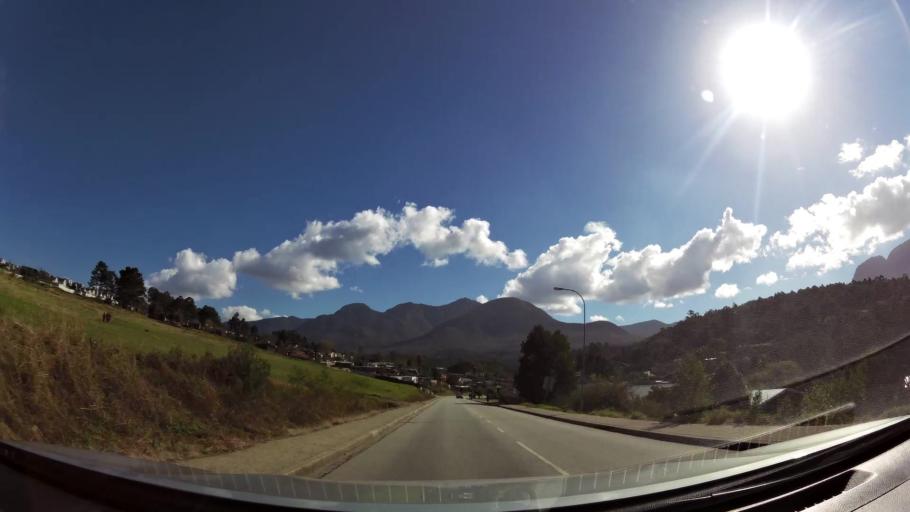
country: ZA
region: Western Cape
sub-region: Eden District Municipality
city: George
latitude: -33.9426
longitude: 22.4116
